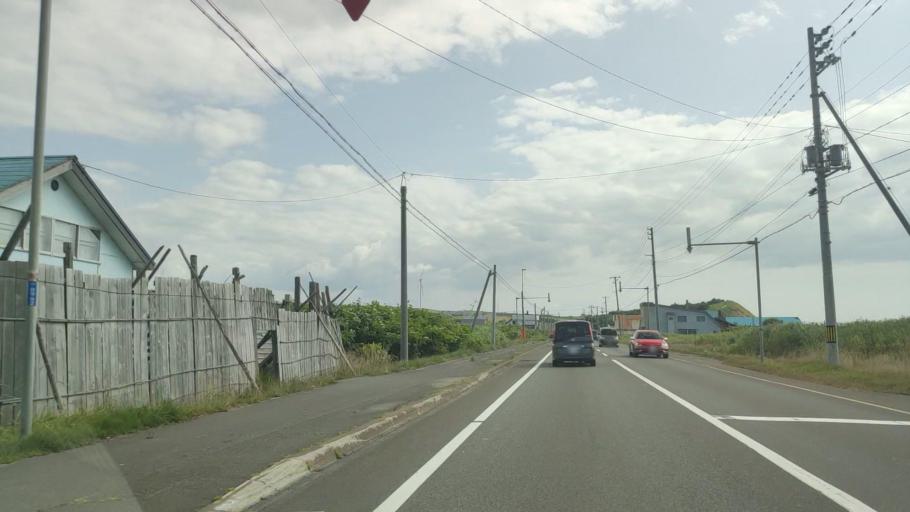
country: JP
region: Hokkaido
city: Rumoi
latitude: 44.2656
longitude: 141.6555
